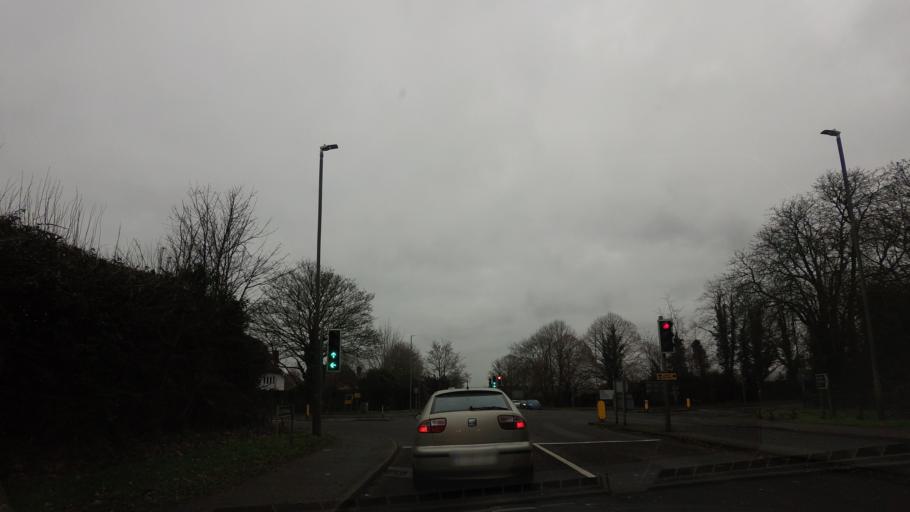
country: GB
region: England
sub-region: Kent
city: Maidstone
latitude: 51.2297
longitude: 0.5127
